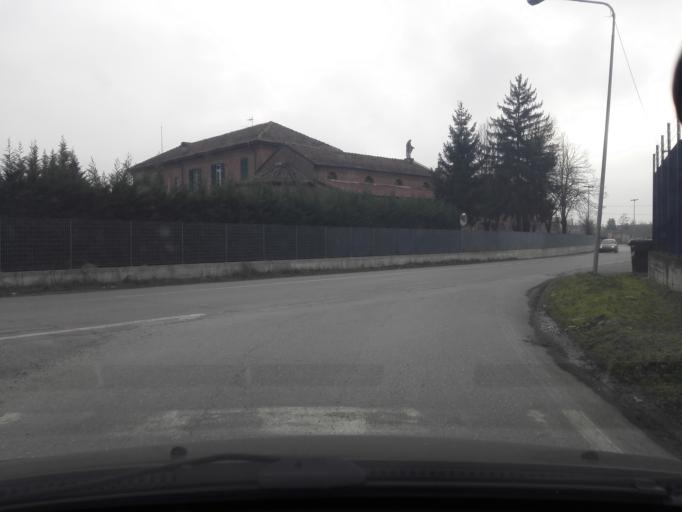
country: IT
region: Piedmont
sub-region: Provincia di Alessandria
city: Bosco Marengo
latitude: 44.8251
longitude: 8.6807
